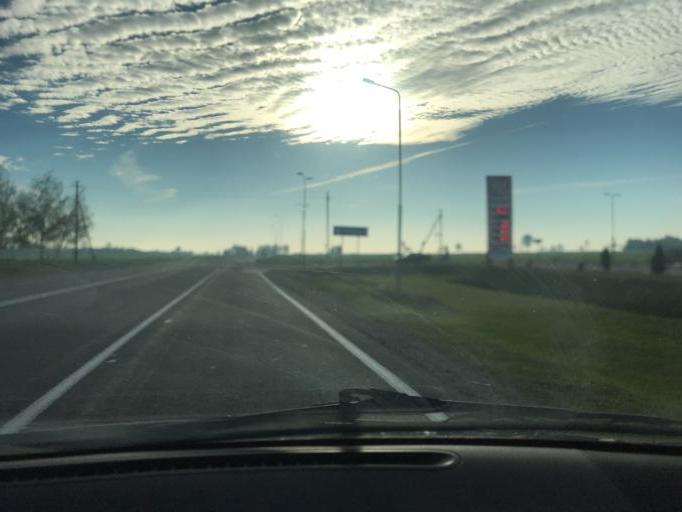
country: BY
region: Brest
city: Drahichyn
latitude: 52.2082
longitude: 25.2180
